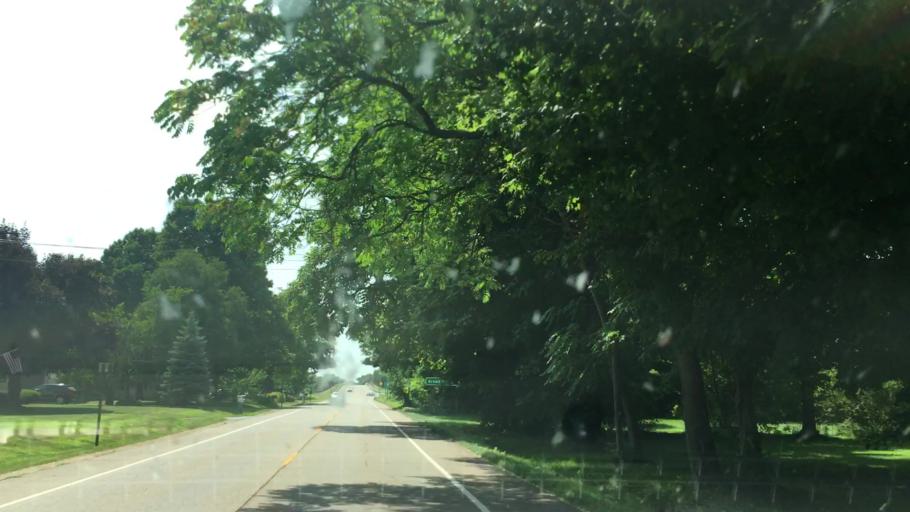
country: US
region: Michigan
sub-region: Allegan County
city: Plainwell
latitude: 42.4645
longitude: -85.6468
